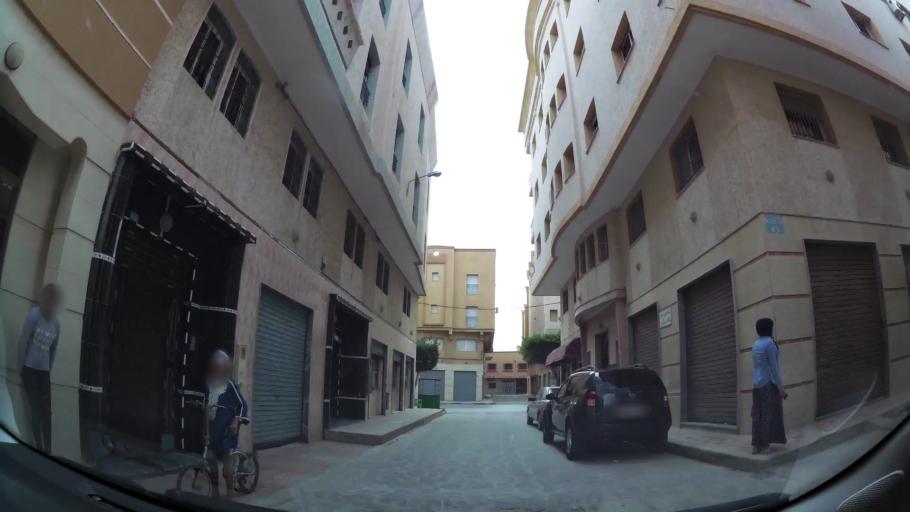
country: MA
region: Oriental
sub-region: Nador
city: Nador
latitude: 35.1633
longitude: -2.9227
